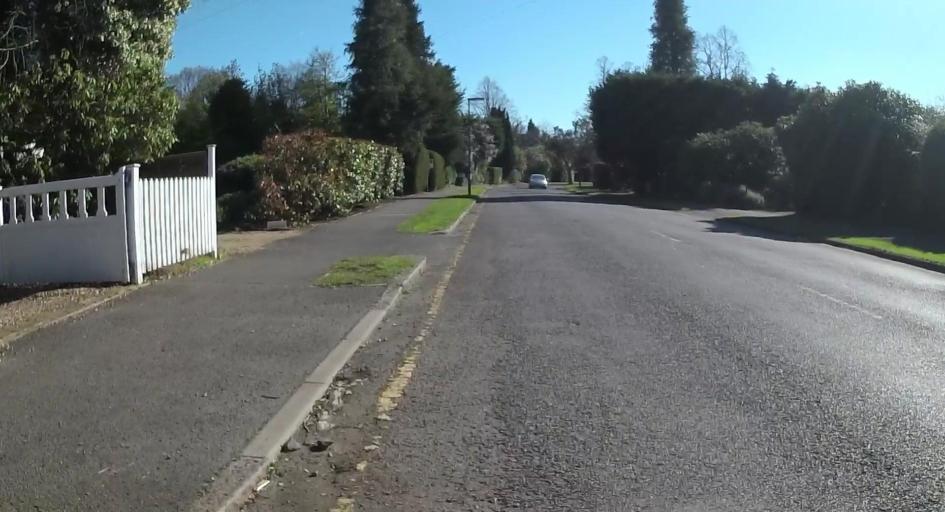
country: GB
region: England
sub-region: Surrey
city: Walton-on-Thames
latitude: 51.3786
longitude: -0.4180
